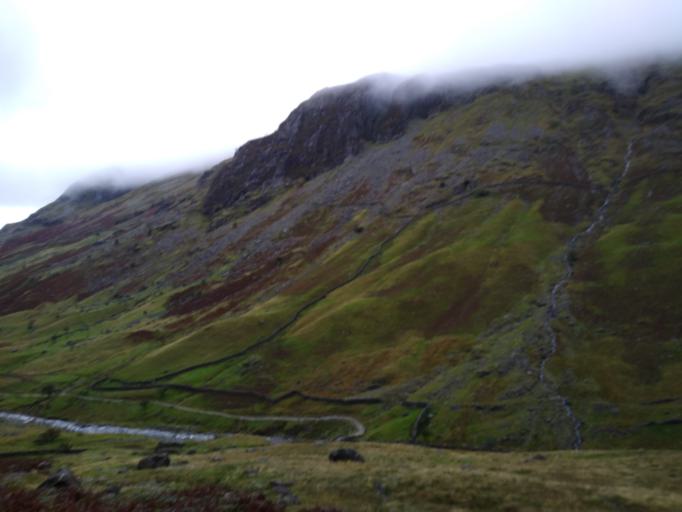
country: GB
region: England
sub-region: Cumbria
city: Keswick
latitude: 54.4871
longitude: -3.1852
